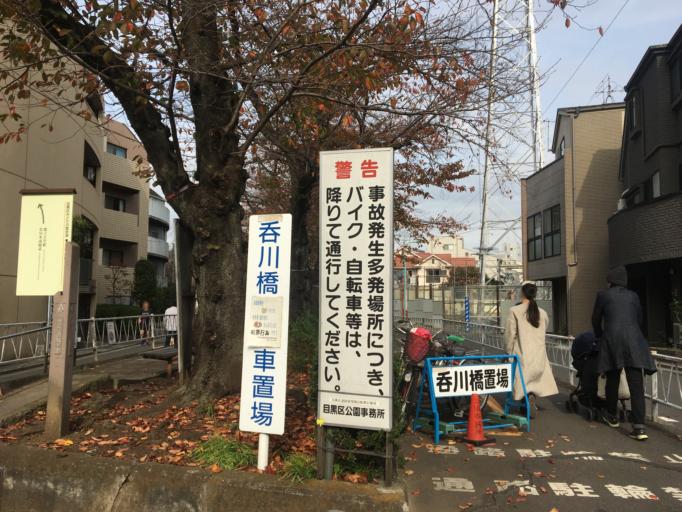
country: JP
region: Tokyo
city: Tokyo
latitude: 35.6158
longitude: 139.6779
